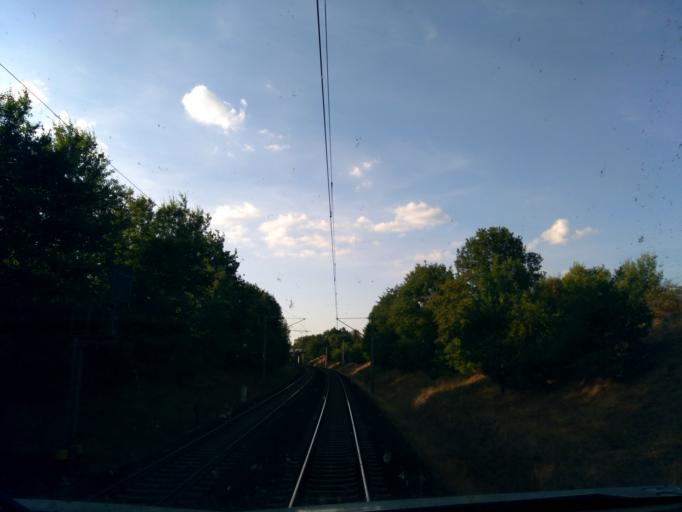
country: DE
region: Mecklenburg-Vorpommern
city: Ludwigslust
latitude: 53.3240
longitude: 11.5065
